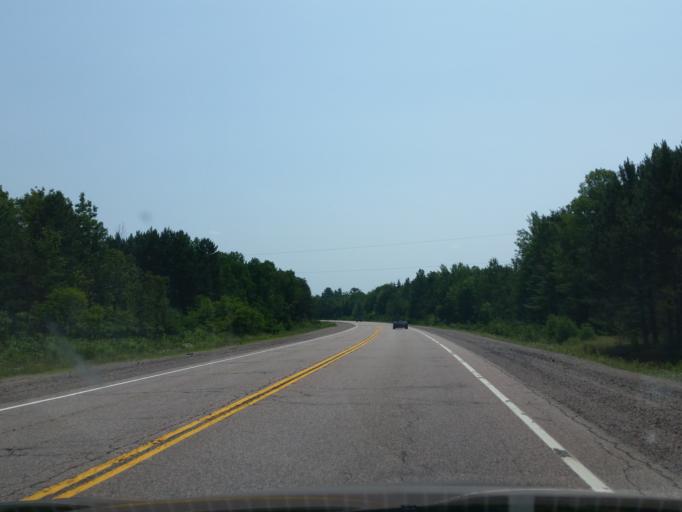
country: CA
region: Ontario
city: Petawawa
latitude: 45.8486
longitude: -77.2770
